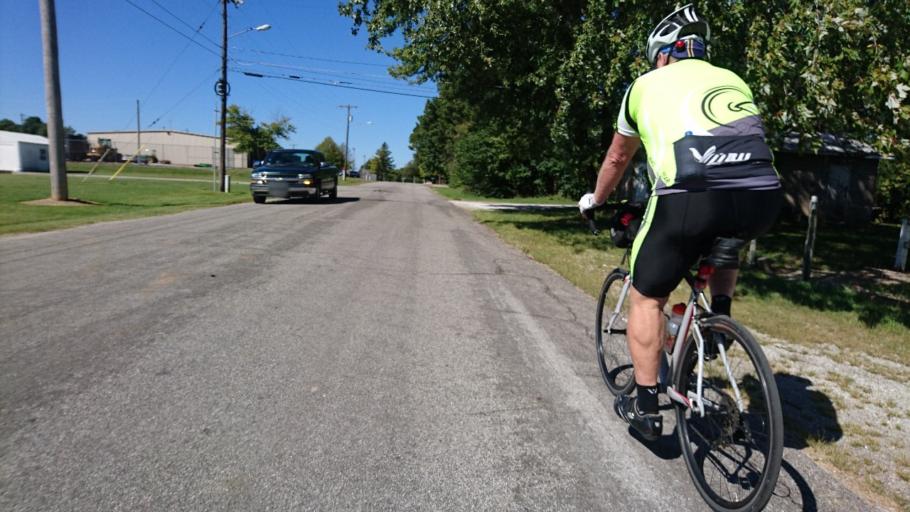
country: US
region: Missouri
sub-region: Jasper County
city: Joplin
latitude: 37.0917
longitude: -94.5489
